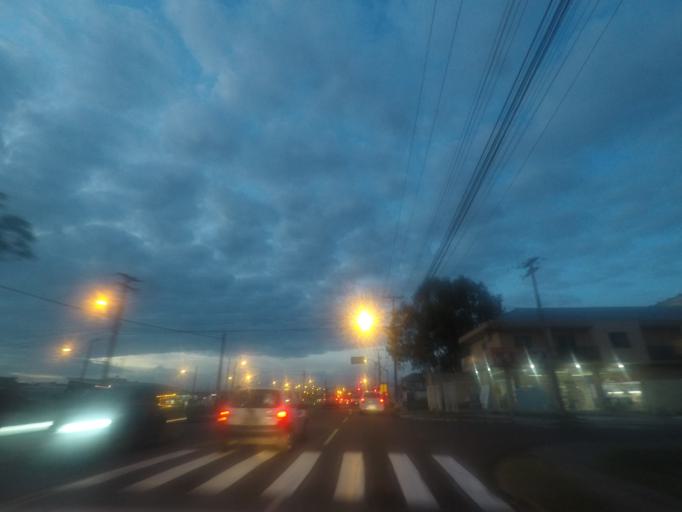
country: BR
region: Parana
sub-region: Pinhais
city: Pinhais
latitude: -25.4038
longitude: -49.1897
